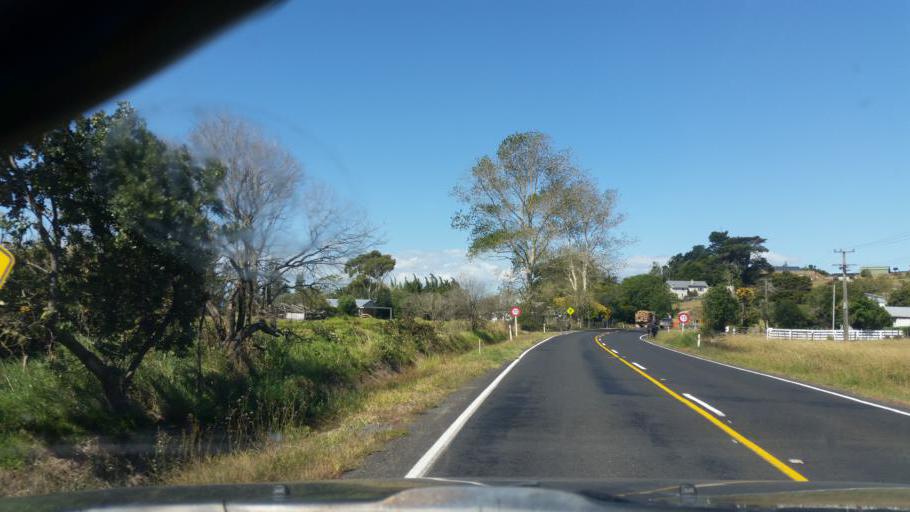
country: NZ
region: Northland
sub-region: Kaipara District
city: Dargaville
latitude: -35.9528
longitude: 173.8517
